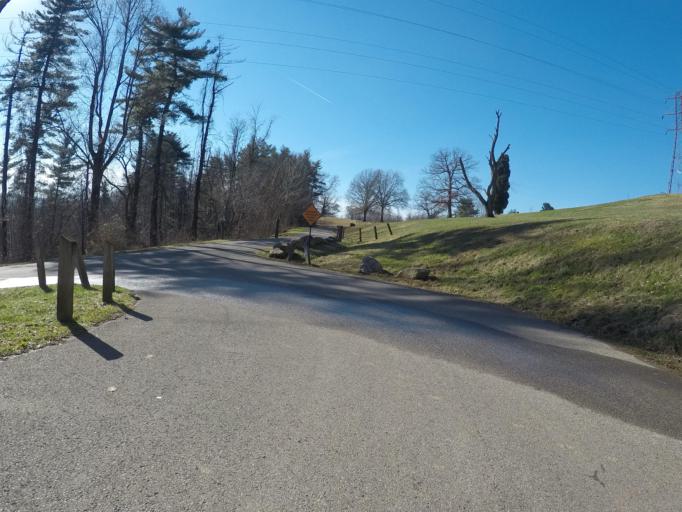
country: US
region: West Virginia
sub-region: Cabell County
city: Huntington
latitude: 38.4201
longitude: -82.3945
